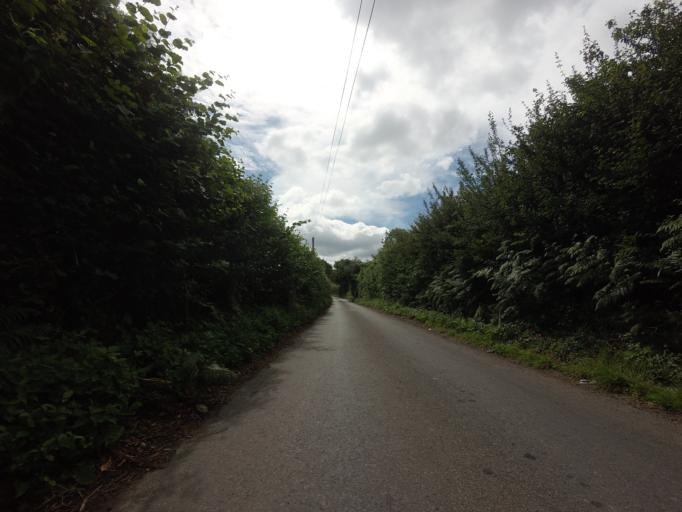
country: GB
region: England
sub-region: Kent
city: Swanley
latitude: 51.3669
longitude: 0.1476
